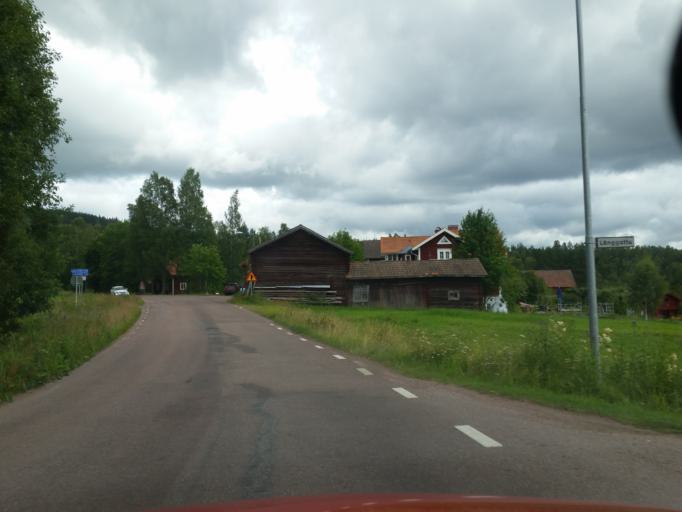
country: SE
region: Dalarna
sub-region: Leksand Municipality
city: Smedby
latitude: 60.7161
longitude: 15.0866
